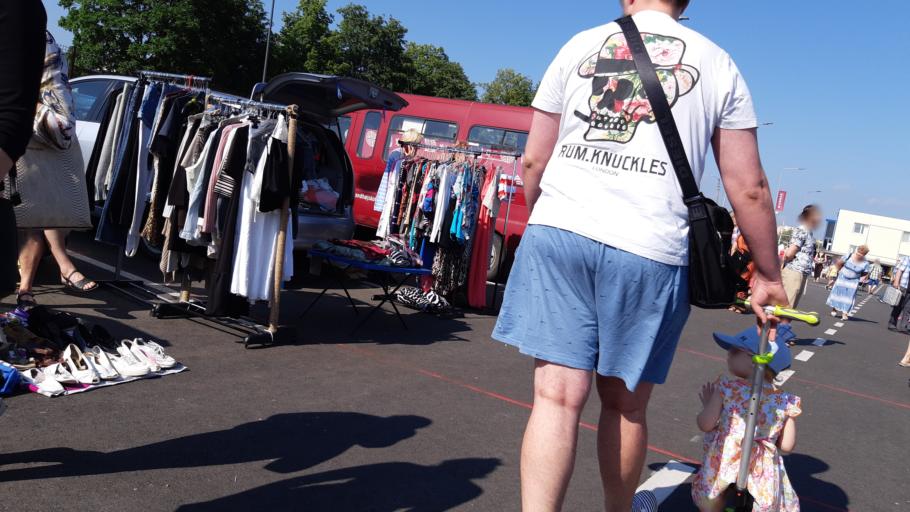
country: LT
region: Kauno apskritis
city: Dainava (Kaunas)
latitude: 54.9136
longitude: 23.9964
